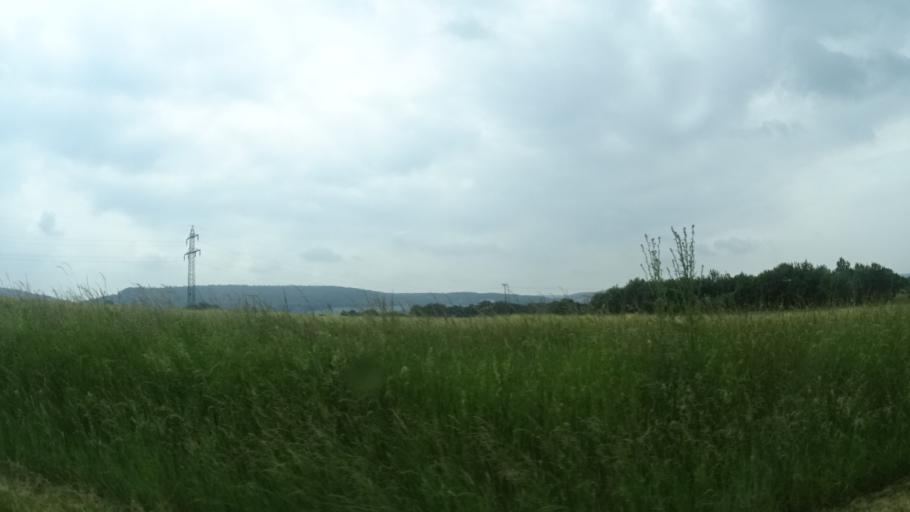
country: DE
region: Hesse
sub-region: Regierungsbezirk Kassel
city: Bad Salzschlirf
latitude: 50.6095
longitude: 9.5066
